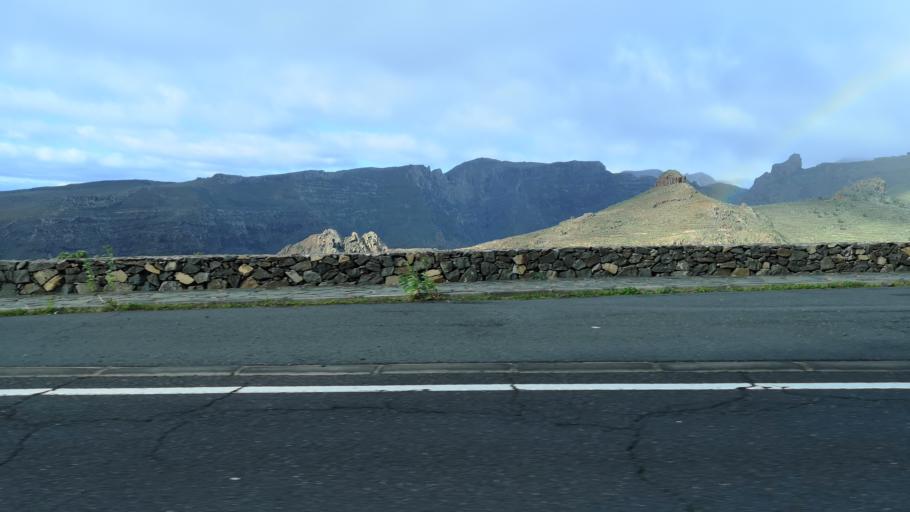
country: ES
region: Canary Islands
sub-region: Provincia de Santa Cruz de Tenerife
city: San Sebastian de la Gomera
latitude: 28.0888
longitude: -17.1507
